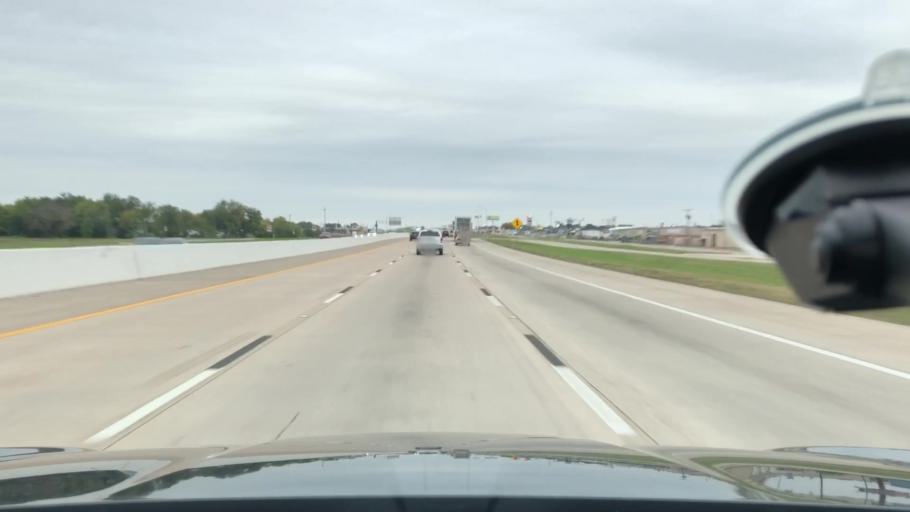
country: US
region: Texas
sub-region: McLennan County
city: Northcrest
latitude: 31.6620
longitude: -97.1003
